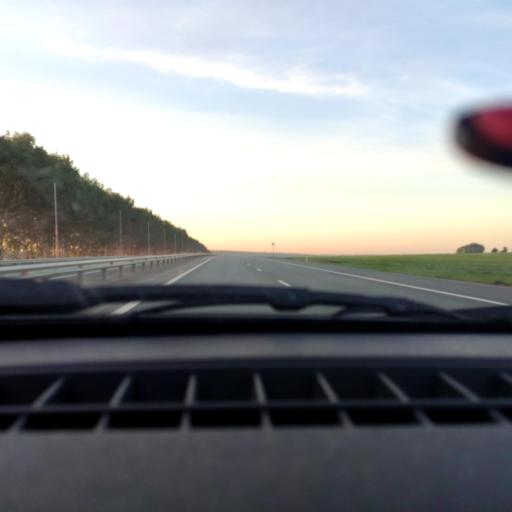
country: RU
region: Bashkortostan
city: Karmaskaly
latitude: 54.3447
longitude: 55.9045
